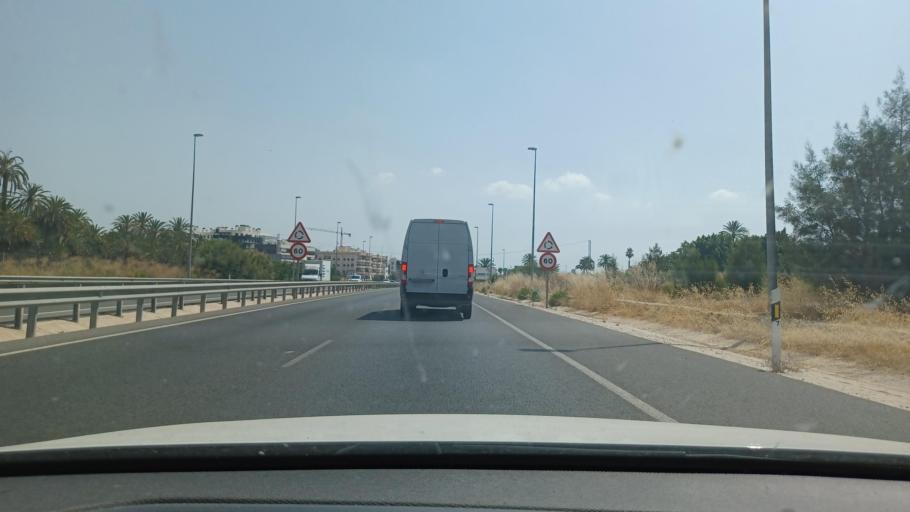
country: ES
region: Valencia
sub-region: Provincia de Alicante
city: Elche
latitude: 38.2589
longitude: -0.6756
